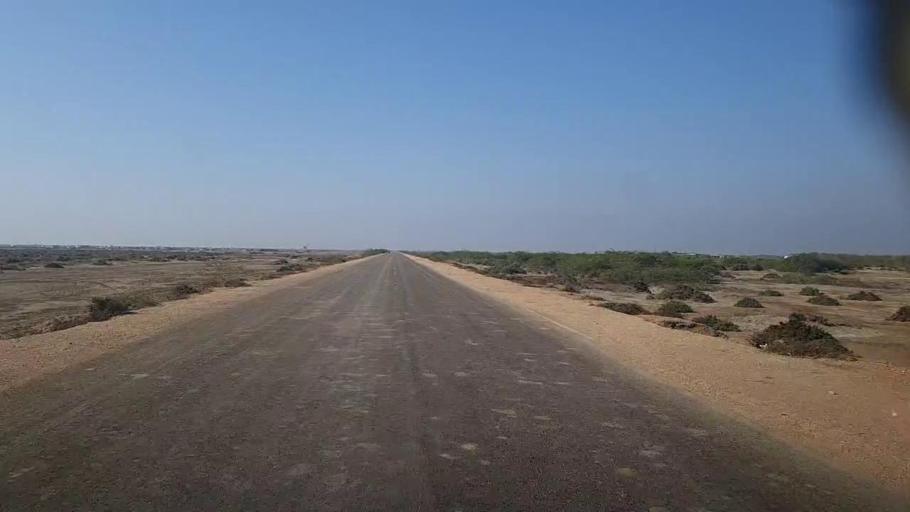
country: PK
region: Sindh
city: Mirpur Sakro
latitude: 24.5579
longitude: 67.4965
